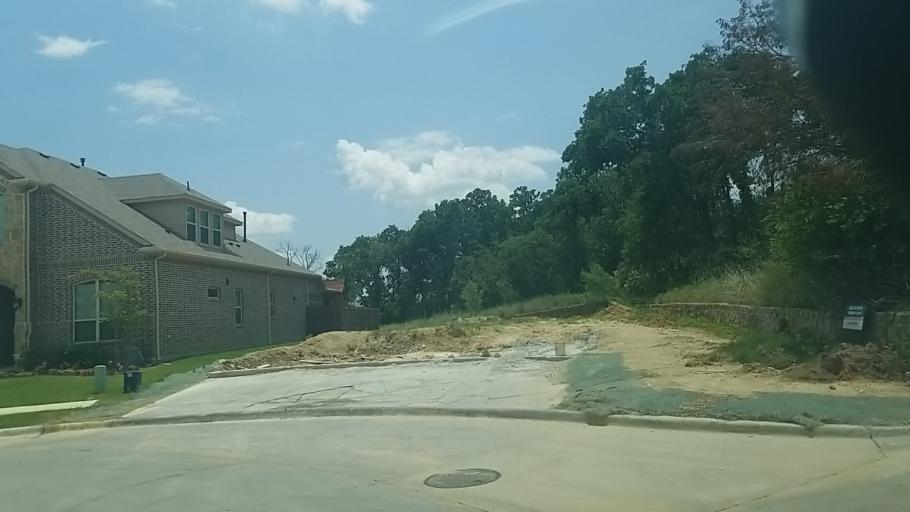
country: US
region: Texas
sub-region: Denton County
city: Corinth
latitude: 33.1663
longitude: -97.1129
